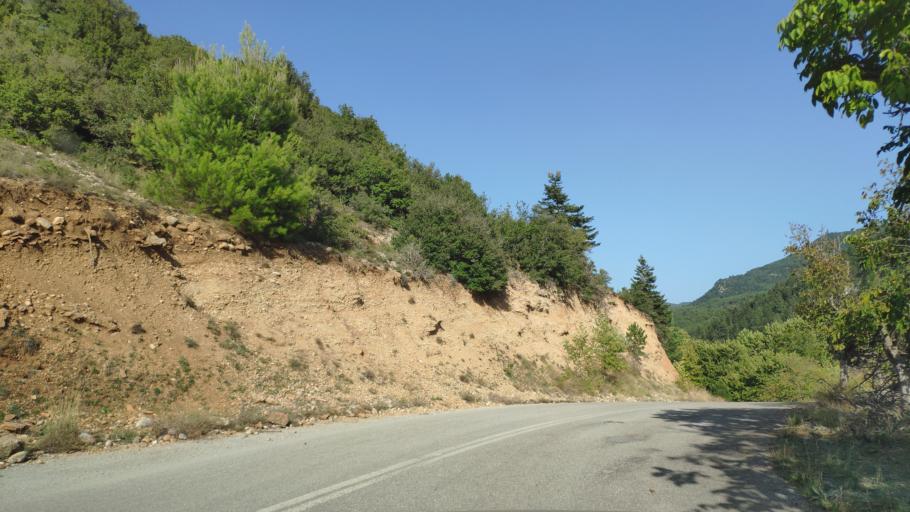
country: GR
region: West Greece
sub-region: Nomos Achaias
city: Aiyira
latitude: 37.9903
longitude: 22.3631
